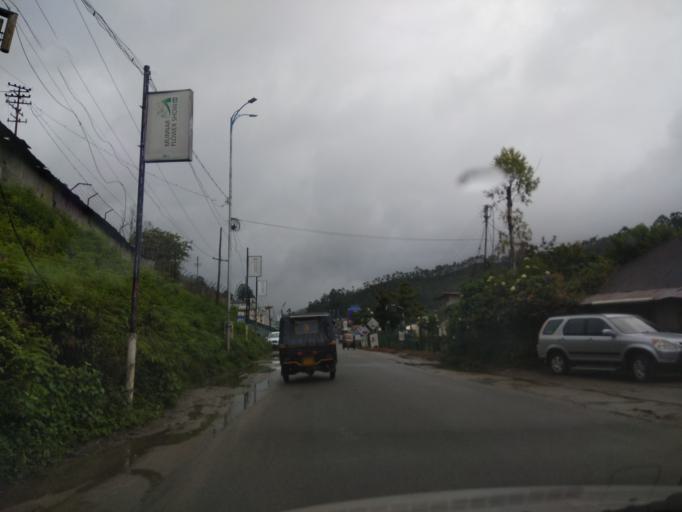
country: IN
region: Kerala
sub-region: Idukki
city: Munnar
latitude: 10.0754
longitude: 77.0631
